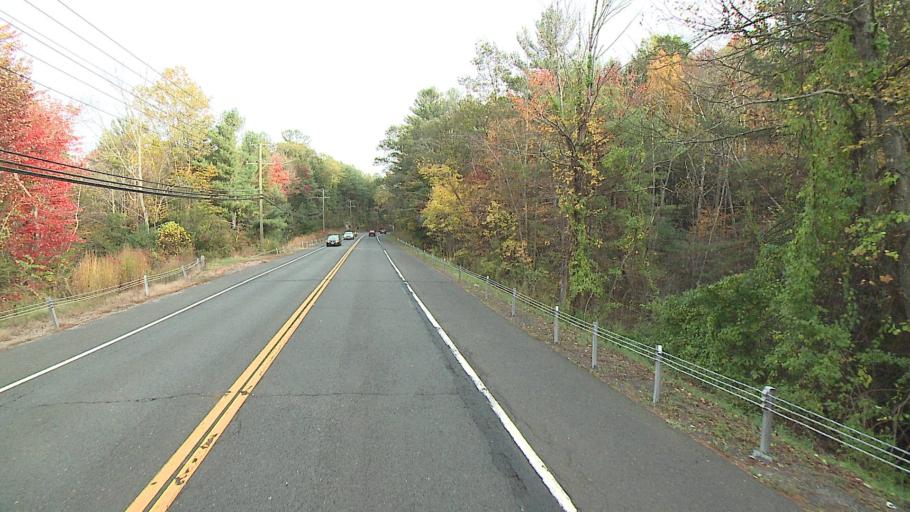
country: US
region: Connecticut
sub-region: Litchfield County
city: New Hartford Center
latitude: 41.9111
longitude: -73.0064
